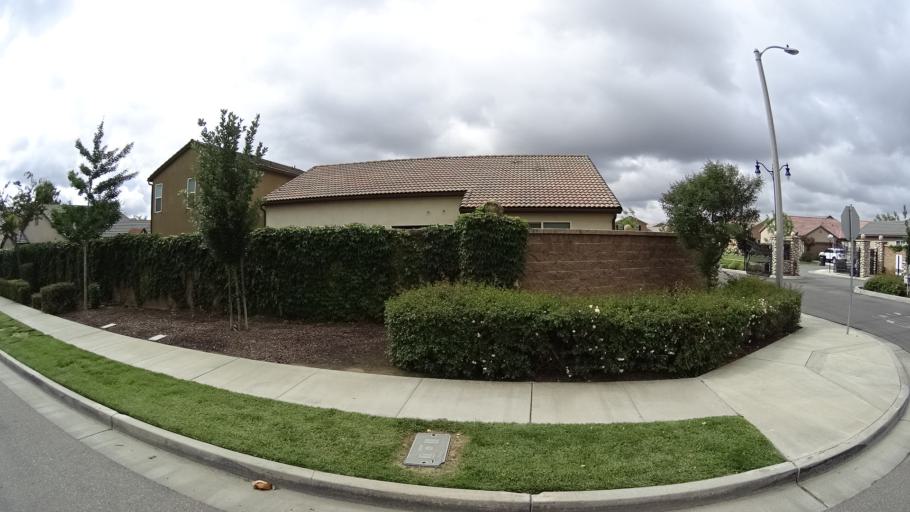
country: US
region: California
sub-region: Kings County
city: Lucerne
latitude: 36.3571
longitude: -119.6748
